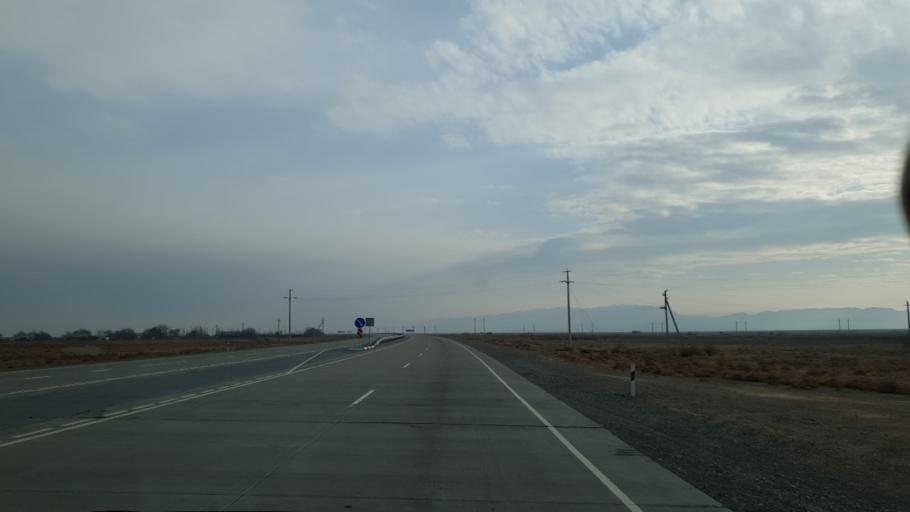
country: KZ
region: Almaty Oblysy
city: Saryozek
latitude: 43.6642
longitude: 78.5690
